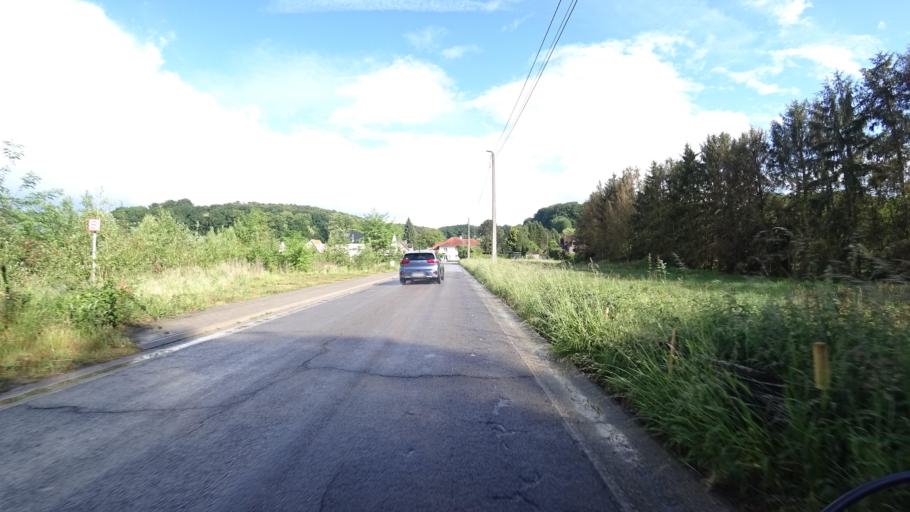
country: BE
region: Wallonia
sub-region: Province du Brabant Wallon
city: Wavre
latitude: 50.7041
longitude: 4.6012
